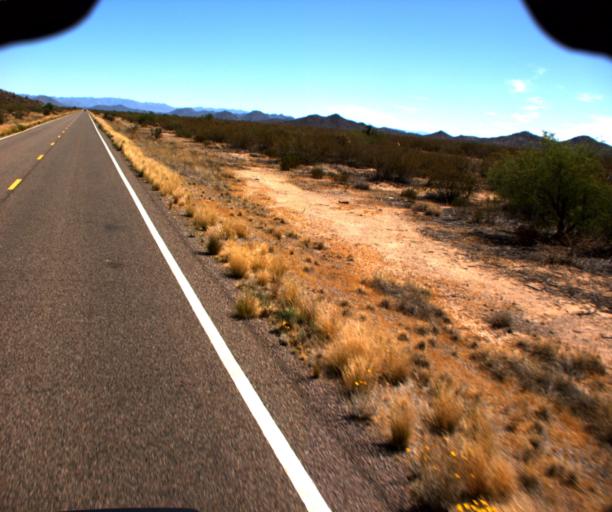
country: US
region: Arizona
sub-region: Yavapai County
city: Congress
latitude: 34.0032
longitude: -113.1177
